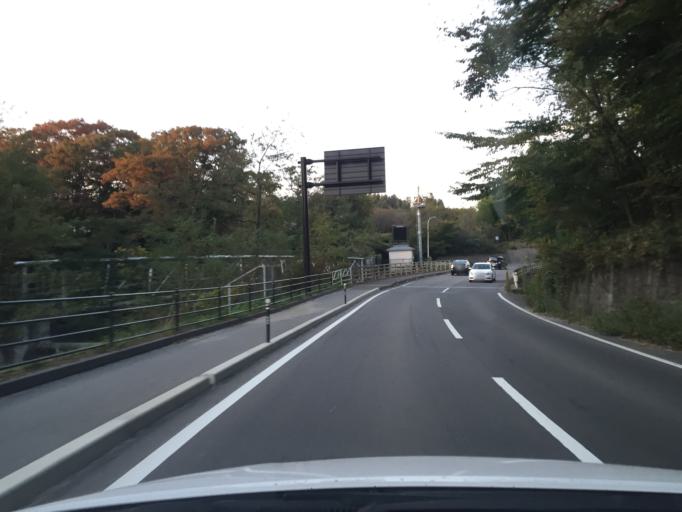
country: JP
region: Fukushima
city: Koriyama
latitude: 37.3728
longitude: 140.4444
